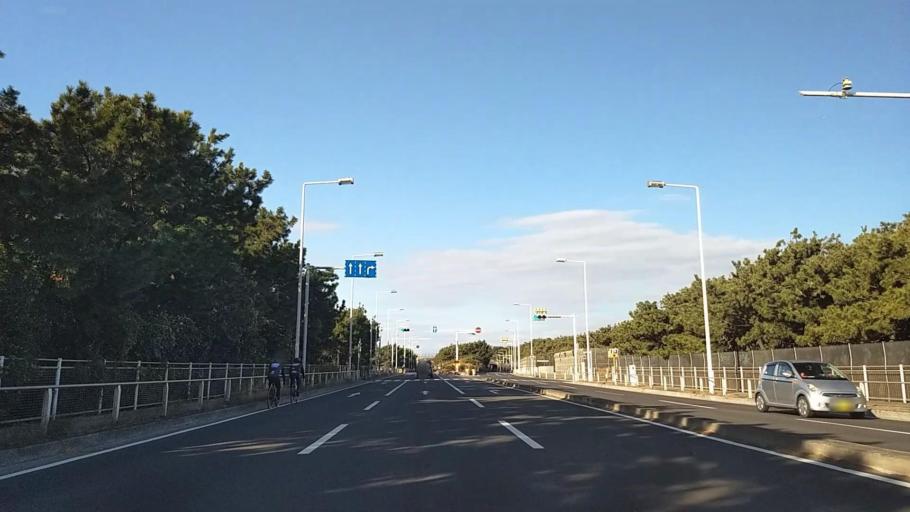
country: JP
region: Kanagawa
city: Fujisawa
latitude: 35.3192
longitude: 139.4517
